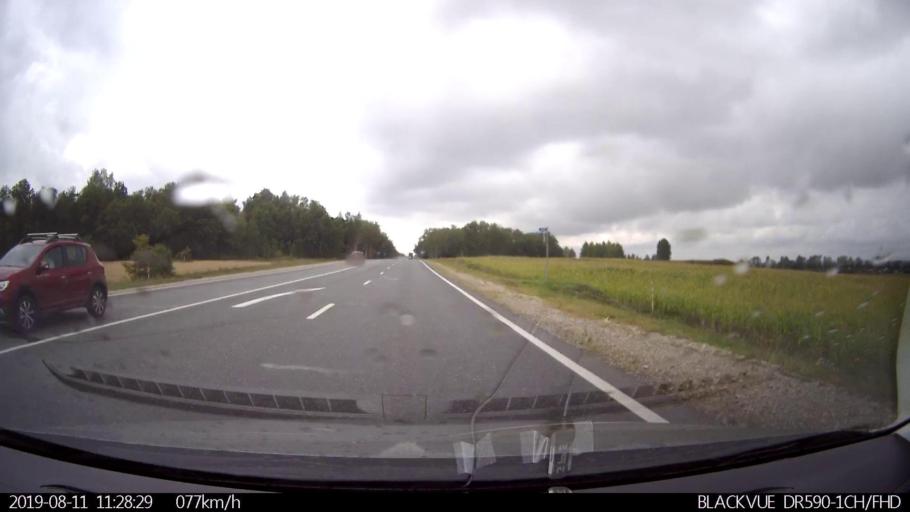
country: RU
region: Ulyanovsk
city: Krasnyy Gulyay
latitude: 54.0820
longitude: 48.2301
